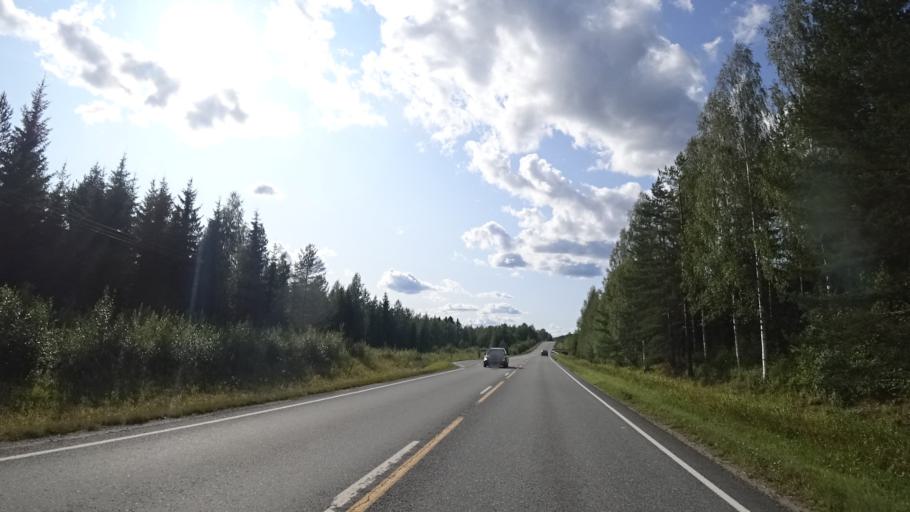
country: FI
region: North Karelia
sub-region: Keski-Karjala
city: Kitee
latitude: 62.0888
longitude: 29.9857
